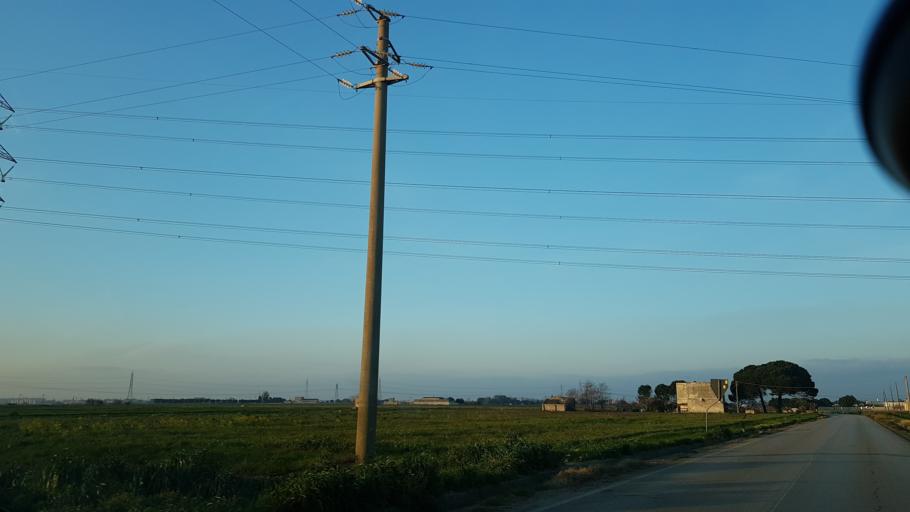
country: IT
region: Apulia
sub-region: Provincia di Brindisi
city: La Rosa
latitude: 40.5918
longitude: 17.9445
